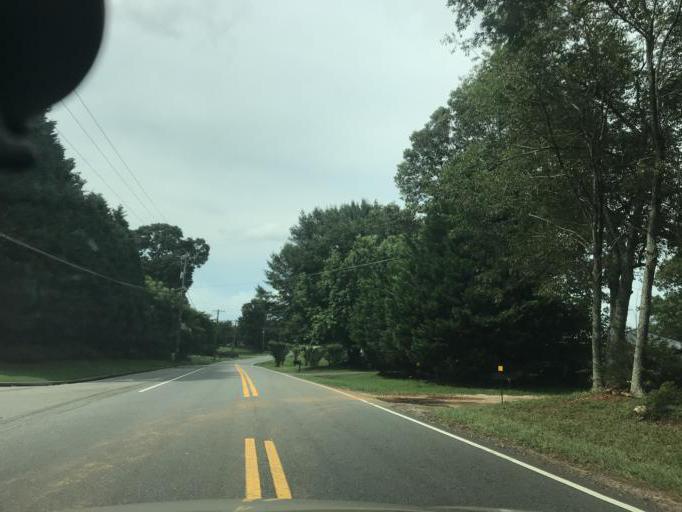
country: US
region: Georgia
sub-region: Forsyth County
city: Cumming
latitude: 34.2609
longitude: -84.2385
